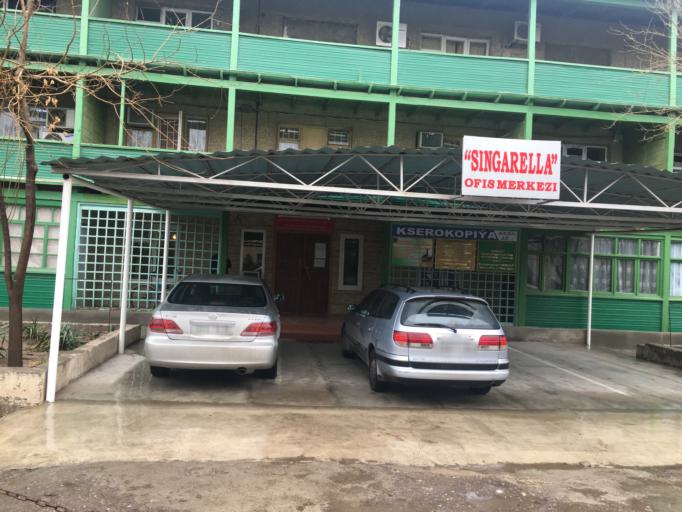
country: TM
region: Mary
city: Mary
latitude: 37.5921
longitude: 61.8301
